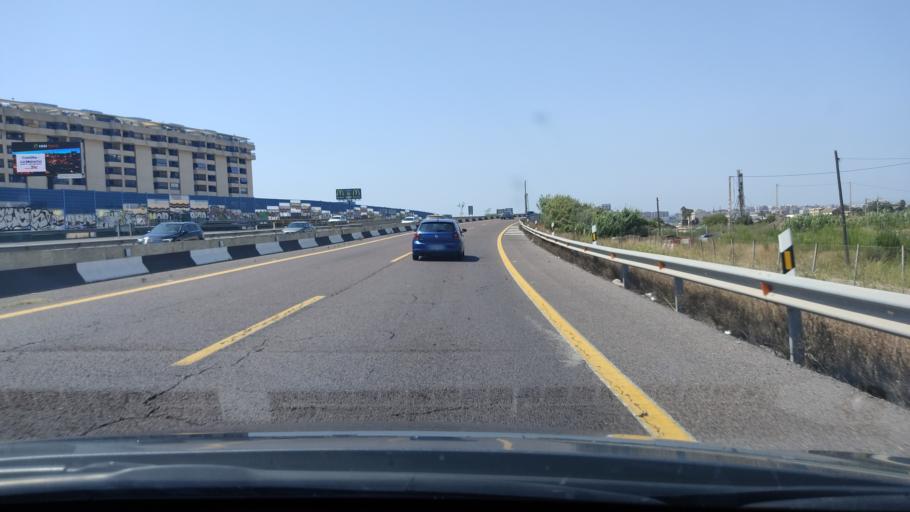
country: ES
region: Valencia
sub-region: Provincia de Valencia
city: Alboraya
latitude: 39.4965
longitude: -0.3275
